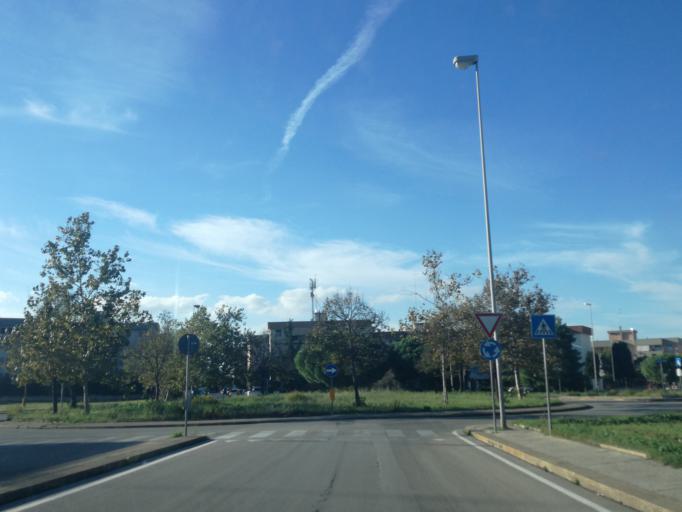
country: IT
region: Apulia
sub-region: Provincia di Bari
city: San Paolo
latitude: 41.1266
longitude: 16.7839
